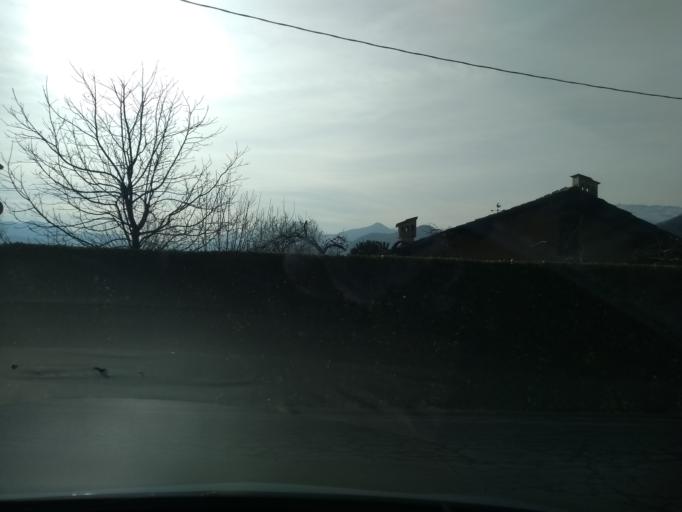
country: IT
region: Piedmont
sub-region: Provincia di Torino
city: Coassolo
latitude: 45.3124
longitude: 7.4787
